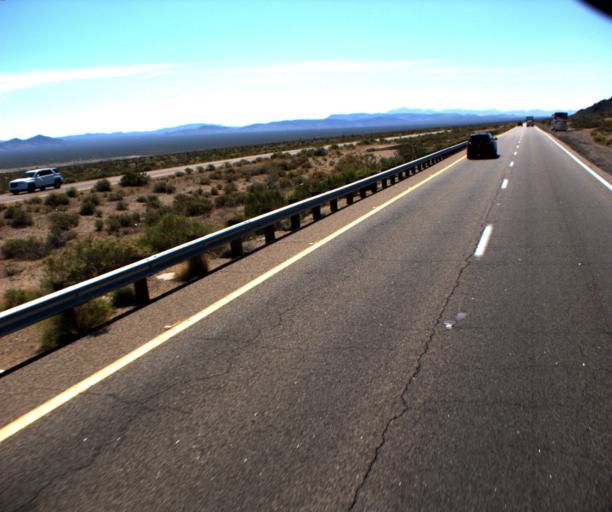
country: US
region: Arizona
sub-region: Mohave County
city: Dolan Springs
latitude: 35.8046
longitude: -114.5390
